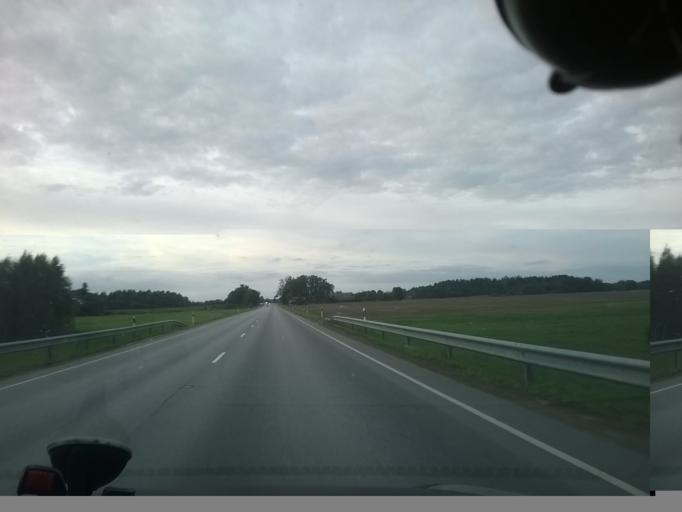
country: EE
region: Vorumaa
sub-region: Voru linn
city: Voru
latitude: 57.9008
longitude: 26.8379
